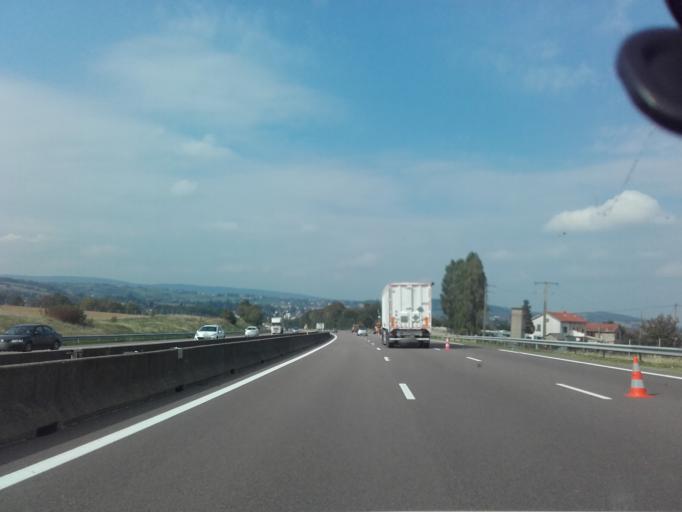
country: FR
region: Bourgogne
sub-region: Departement de Saone-et-Loire
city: Tournus
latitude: 46.5446
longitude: 4.9169
